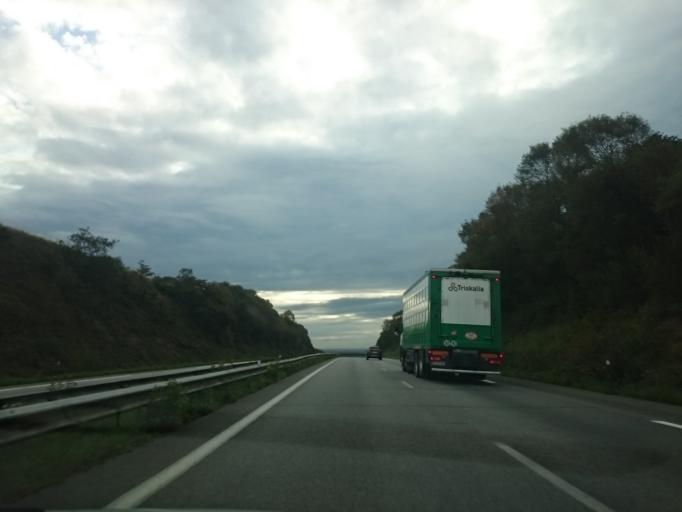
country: FR
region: Brittany
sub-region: Departement du Finistere
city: Le Faou
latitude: 48.2816
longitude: -4.1343
